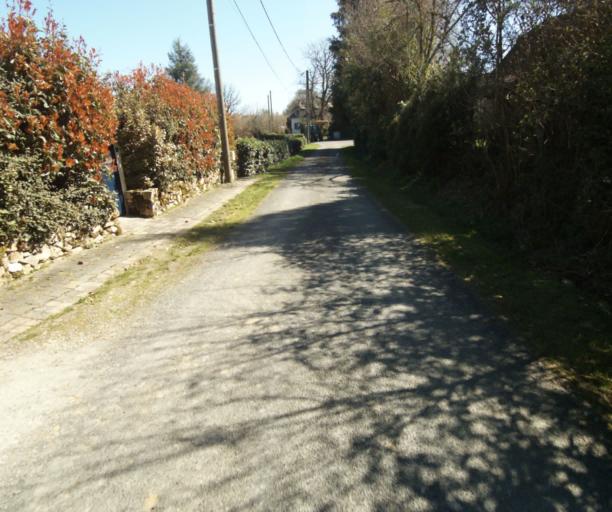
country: FR
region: Limousin
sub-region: Departement de la Correze
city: Saint-Clement
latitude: 45.3205
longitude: 1.6667
